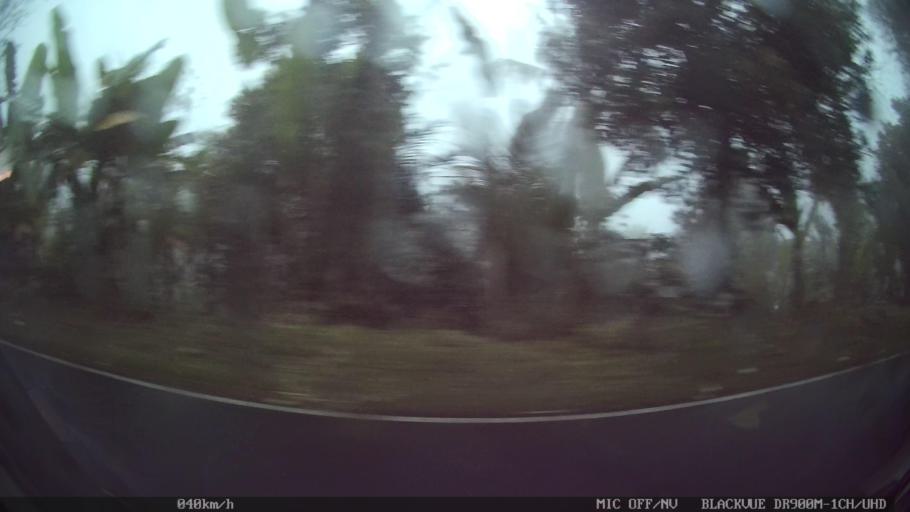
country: ID
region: Bali
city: Banjar Taro Kelod
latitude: -8.3311
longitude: 115.2870
